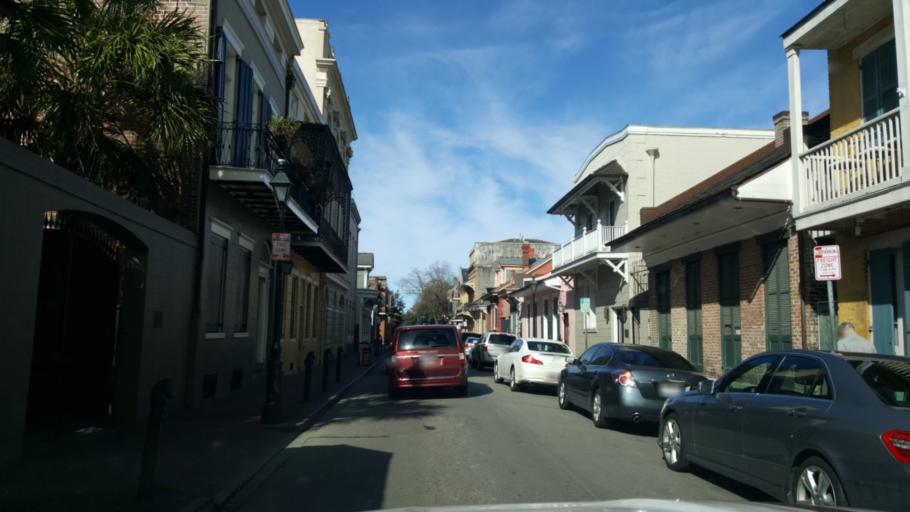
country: US
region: Louisiana
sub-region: Orleans Parish
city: New Orleans
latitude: 29.9577
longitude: -90.0680
